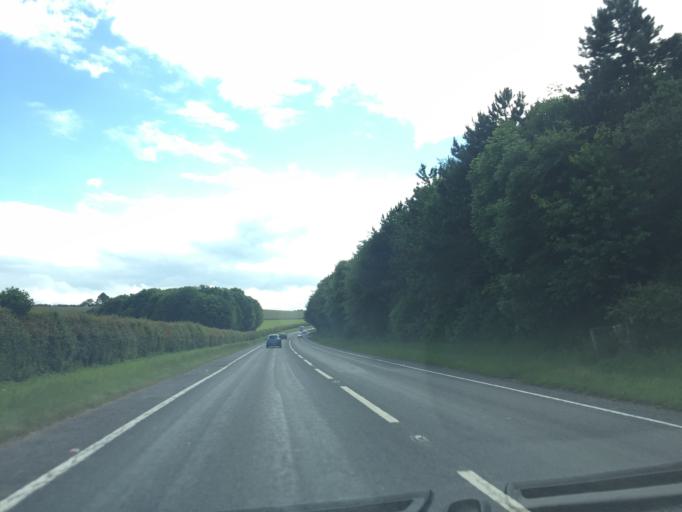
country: GB
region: England
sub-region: Dorset
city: Dorchester
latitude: 50.7048
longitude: -2.4247
